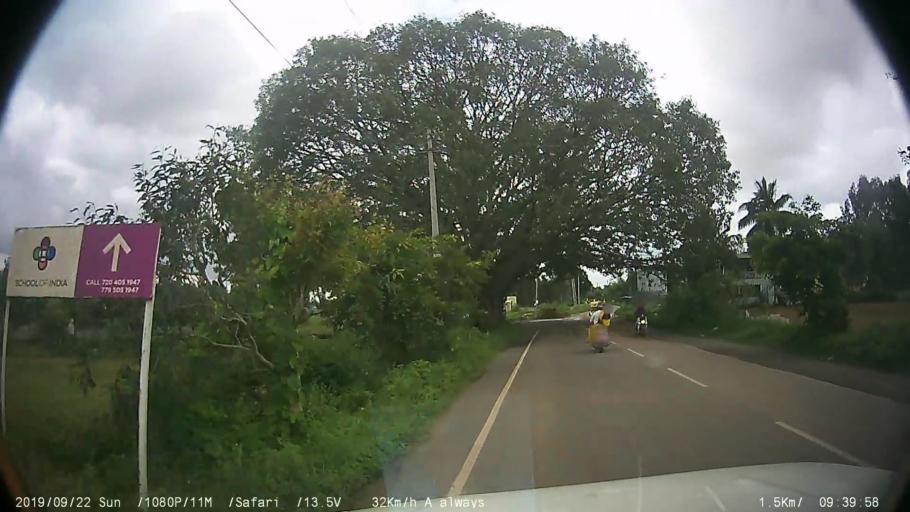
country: IN
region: Karnataka
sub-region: Bangalore Urban
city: Anekal
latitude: 12.8136
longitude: 77.6277
